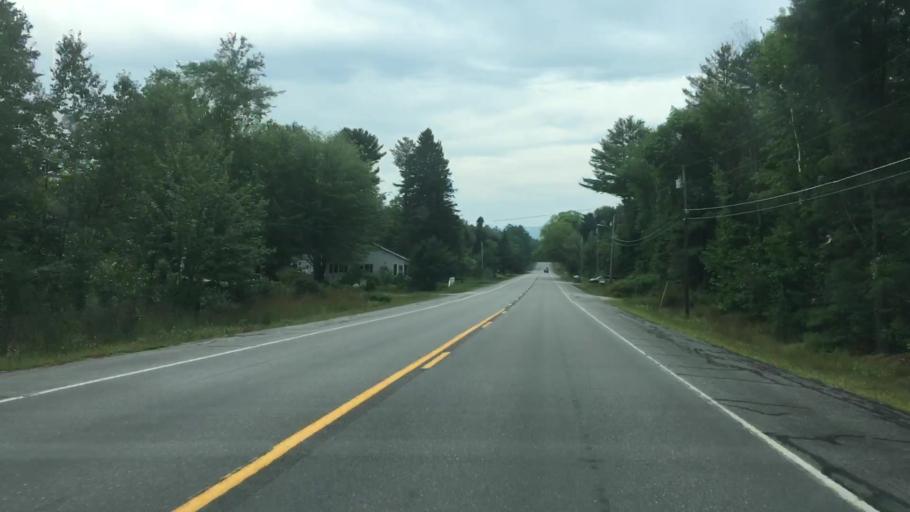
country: US
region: Maine
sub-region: Oxford County
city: Bethel
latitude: 44.4854
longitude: -70.7163
